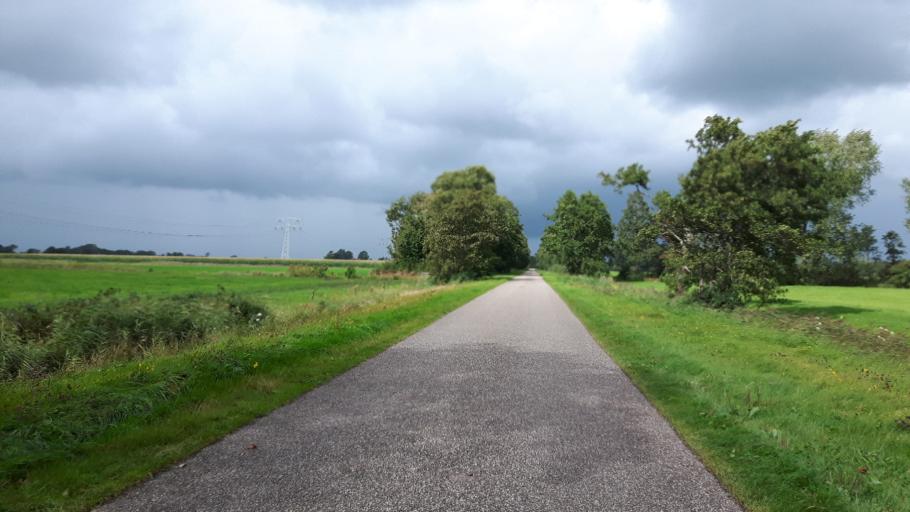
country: NL
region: Friesland
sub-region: Gemeente Dantumadiel
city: Broeksterwald
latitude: 53.2666
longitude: 5.9859
